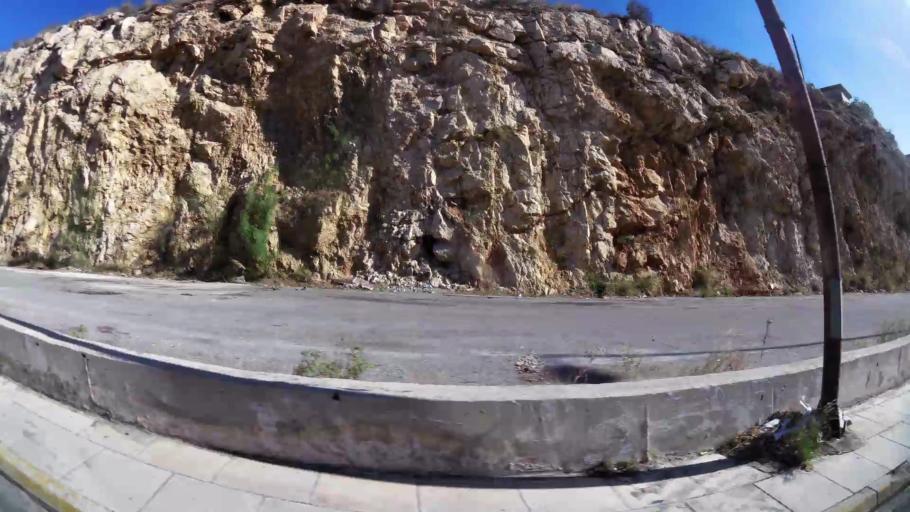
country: GR
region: Attica
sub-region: Nomos Piraios
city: Keratsini
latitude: 37.9686
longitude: 23.6074
